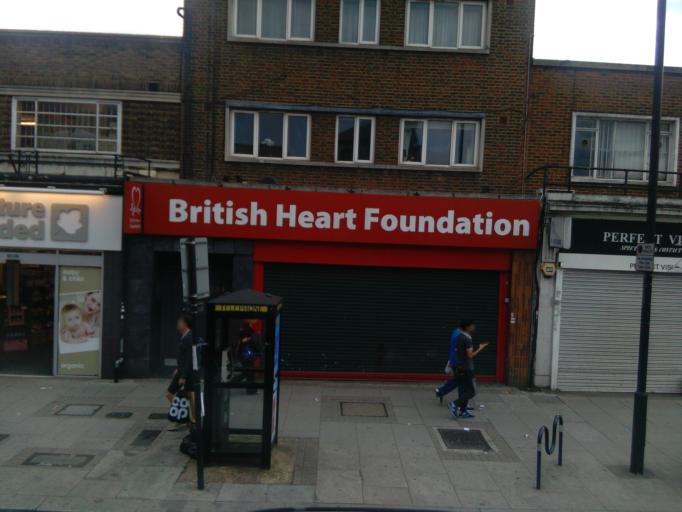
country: GB
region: England
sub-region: Greater London
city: Brixton Hill
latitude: 51.4442
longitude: -0.1524
